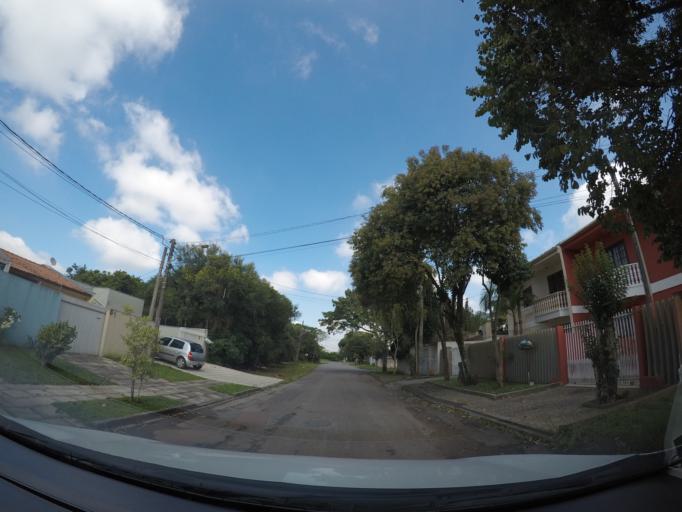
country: BR
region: Parana
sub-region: Sao Jose Dos Pinhais
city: Sao Jose dos Pinhais
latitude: -25.4927
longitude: -49.2260
